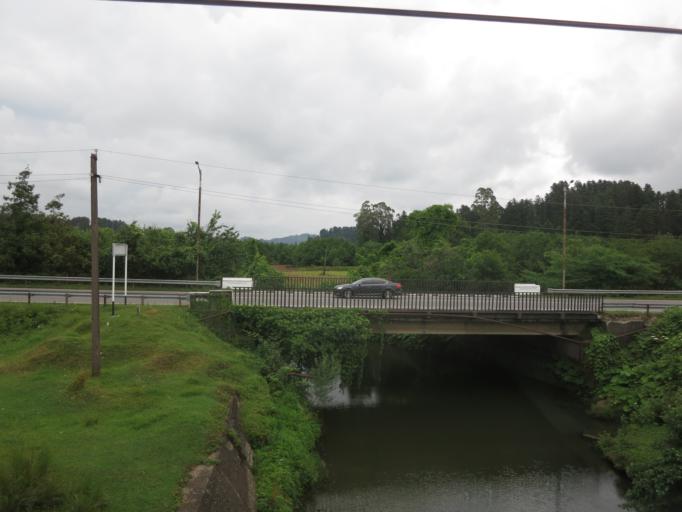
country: GE
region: Guria
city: Urek'i
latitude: 41.9869
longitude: 41.7829
